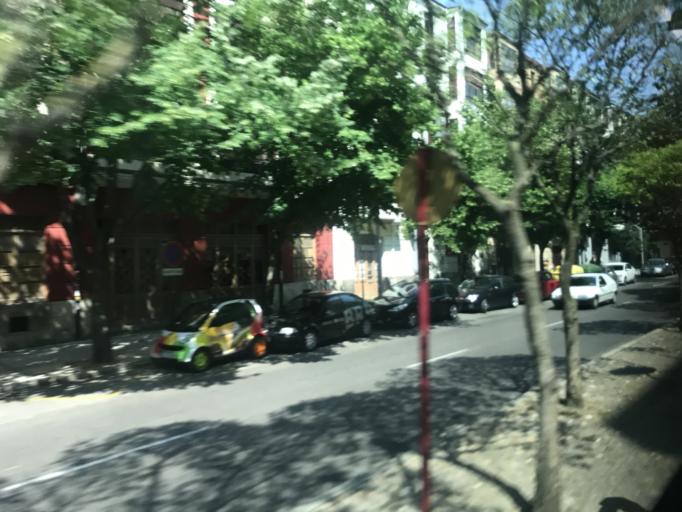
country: ES
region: Castille and Leon
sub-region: Provincia de Palencia
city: Palencia
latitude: 42.0123
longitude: -4.5307
